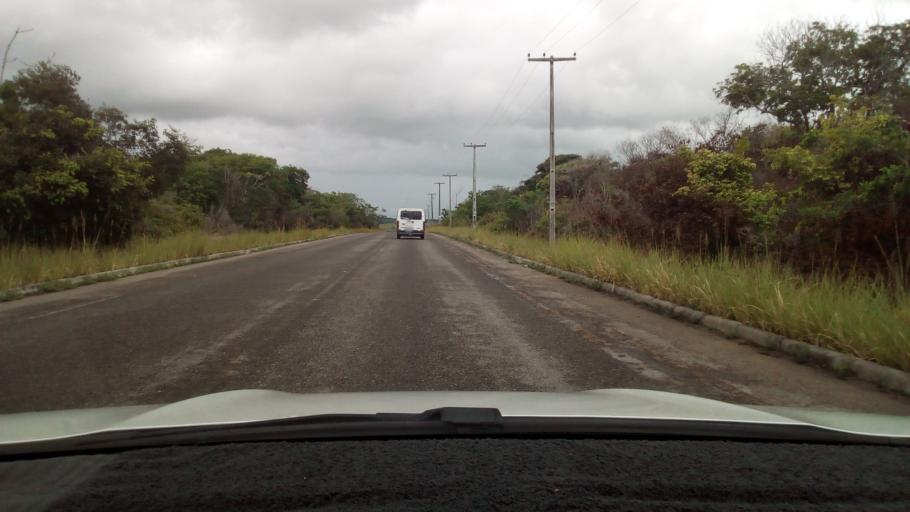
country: BR
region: Paraiba
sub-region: Pitimbu
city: Pitimbu
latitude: -7.3505
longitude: -34.8046
